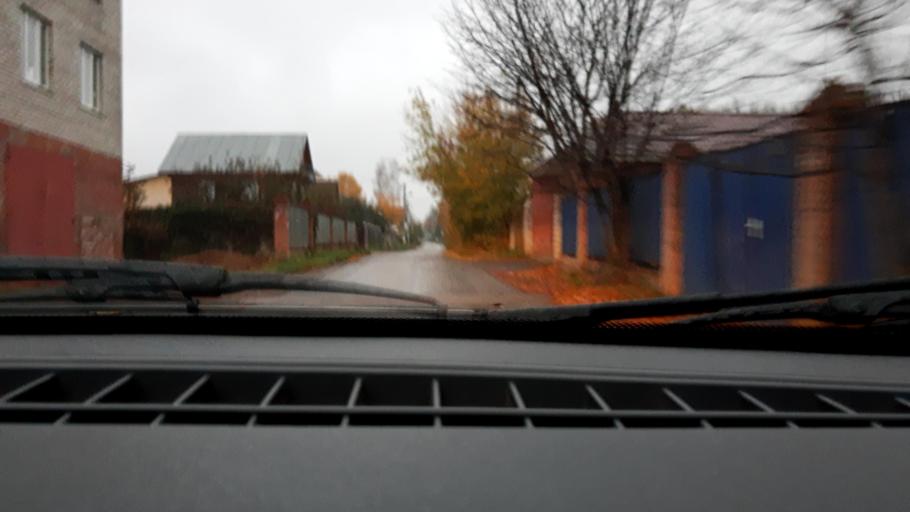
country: RU
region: Bashkortostan
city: Mikhaylovka
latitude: 54.7838
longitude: 55.8986
